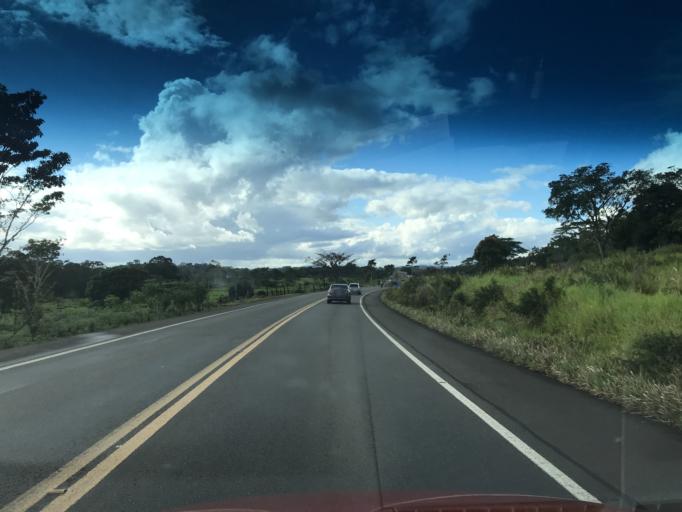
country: BR
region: Bahia
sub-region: Ibirapitanga
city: Ibirapitanga
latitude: -14.1632
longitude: -39.3288
